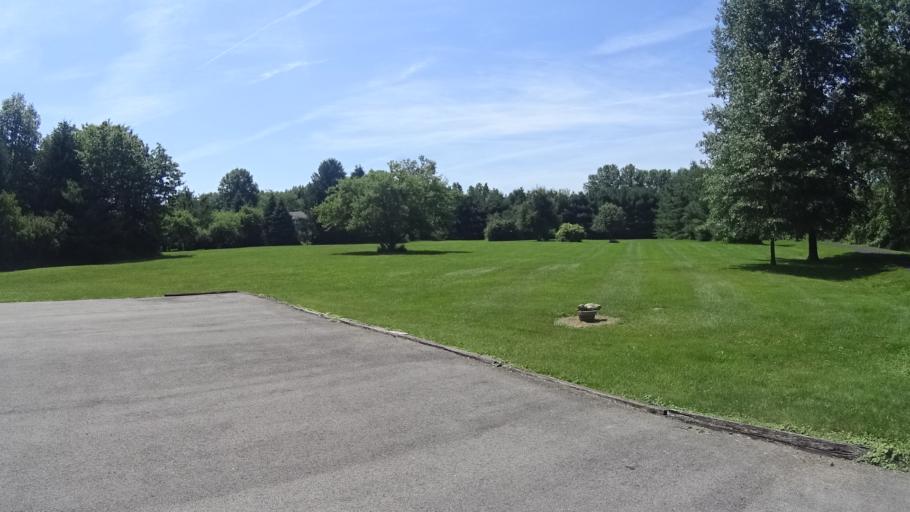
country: US
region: Ohio
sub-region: Lorain County
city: Vermilion
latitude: 41.3665
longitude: -82.4498
